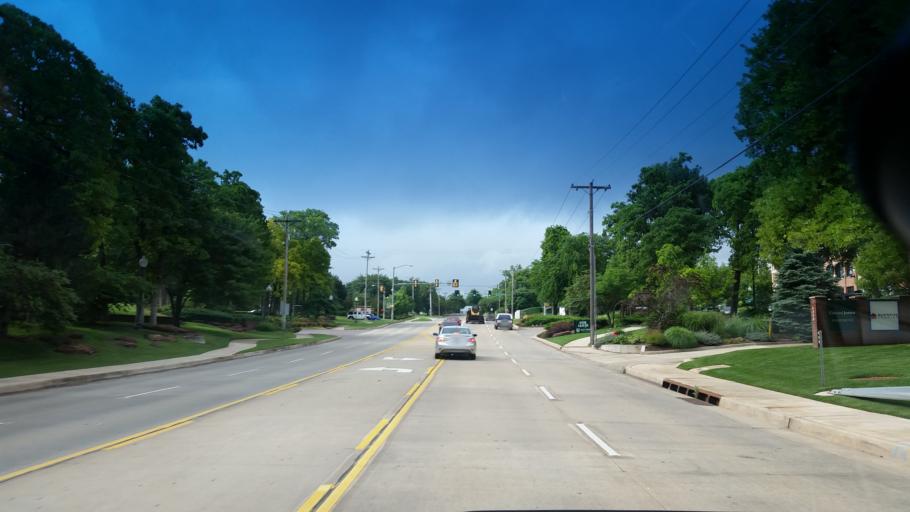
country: US
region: Oklahoma
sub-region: Oklahoma County
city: Edmond
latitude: 35.6396
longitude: -97.4605
